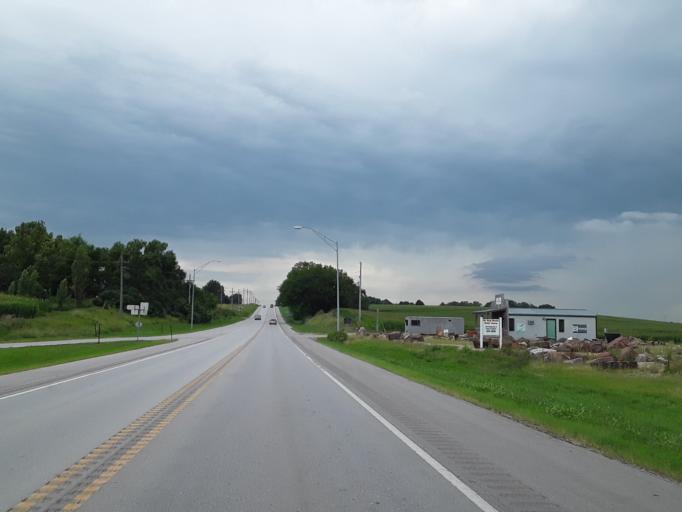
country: US
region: Nebraska
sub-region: Saunders County
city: Yutan
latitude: 41.2338
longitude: -96.3976
